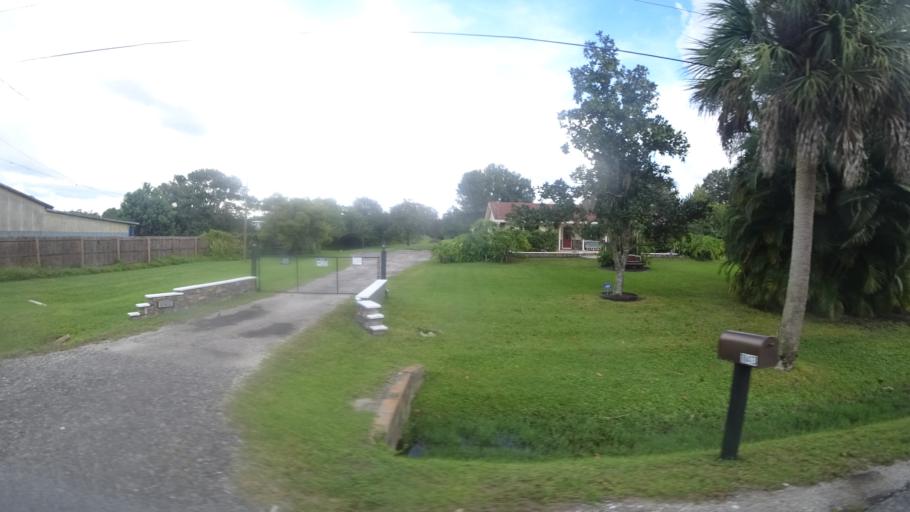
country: US
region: Florida
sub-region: Manatee County
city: Memphis
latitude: 27.6077
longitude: -82.5356
